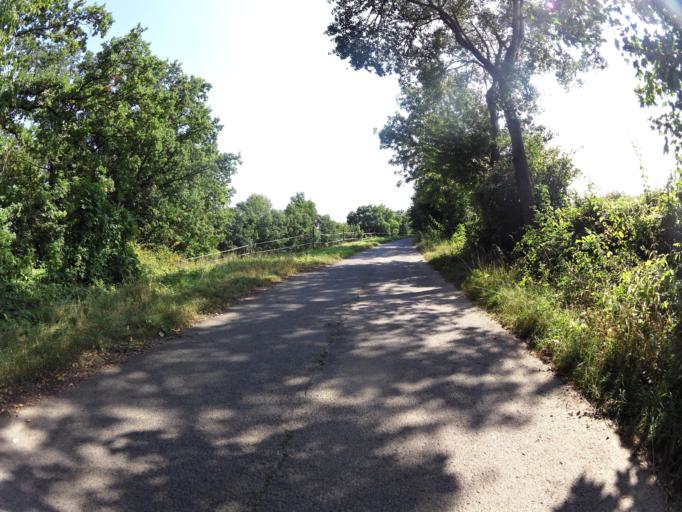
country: DE
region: Bavaria
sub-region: Regierungsbezirk Unterfranken
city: Sommerach
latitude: 49.8337
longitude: 10.1723
